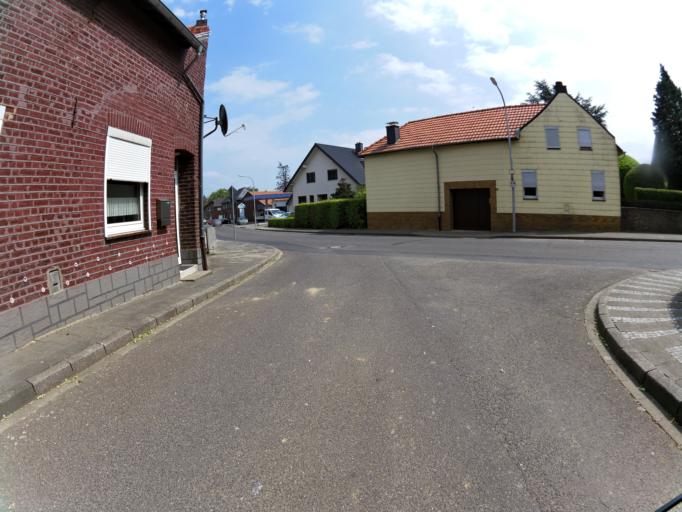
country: DE
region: North Rhine-Westphalia
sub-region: Regierungsbezirk Koln
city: Heinsberg
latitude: 51.0208
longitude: 6.1281
